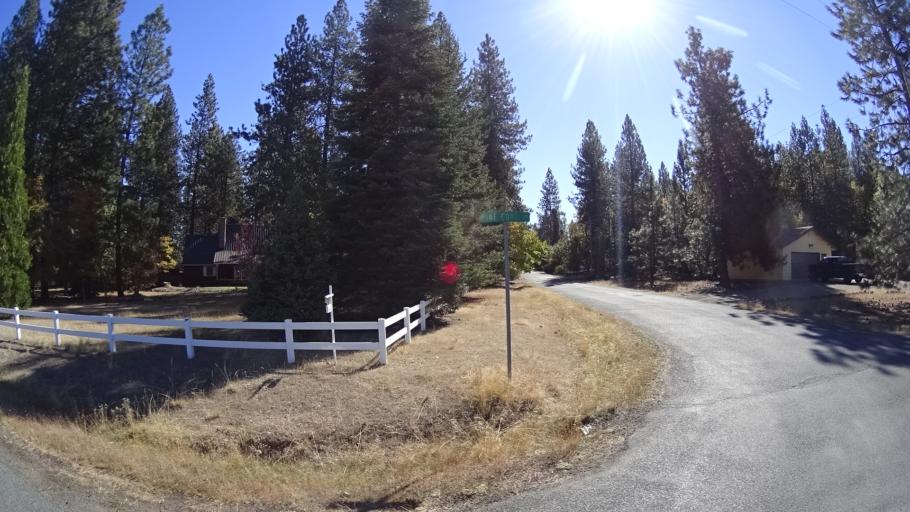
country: US
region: California
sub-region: Siskiyou County
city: Yreka
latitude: 41.5242
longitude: -122.9199
